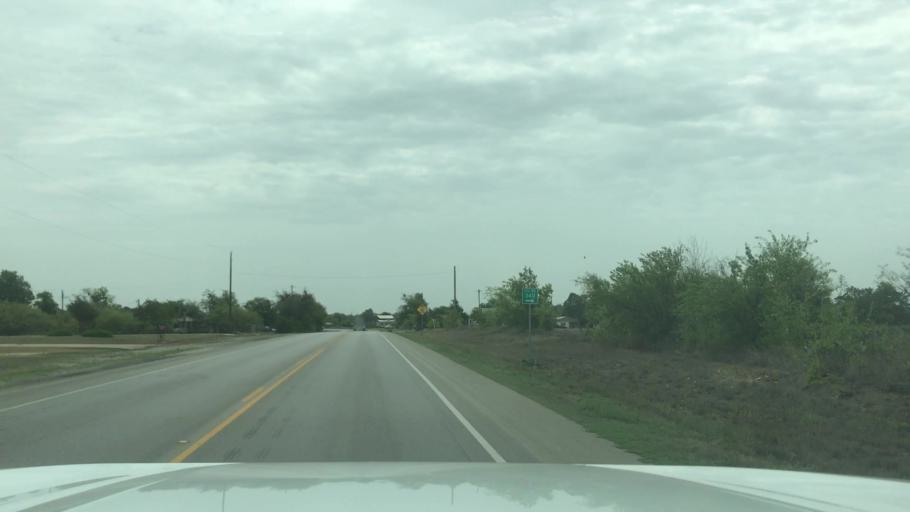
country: US
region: Texas
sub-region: Erath County
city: Dublin
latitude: 32.0903
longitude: -98.3608
